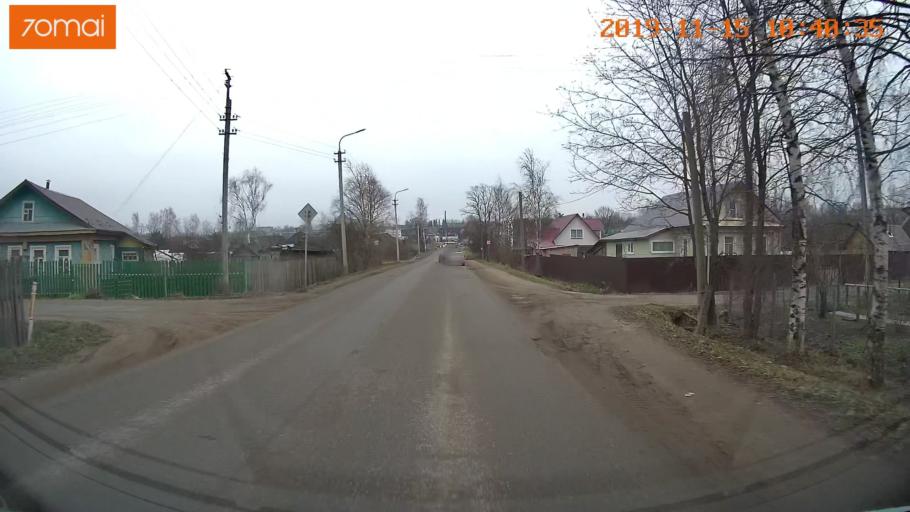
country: RU
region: Vologda
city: Sheksna
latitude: 59.2132
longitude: 38.5096
